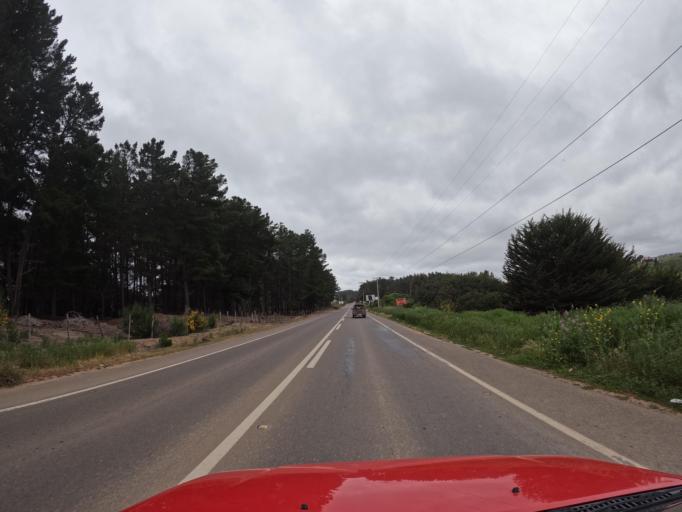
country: CL
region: O'Higgins
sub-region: Provincia de Colchagua
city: Santa Cruz
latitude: -34.4558
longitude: -72.0267
